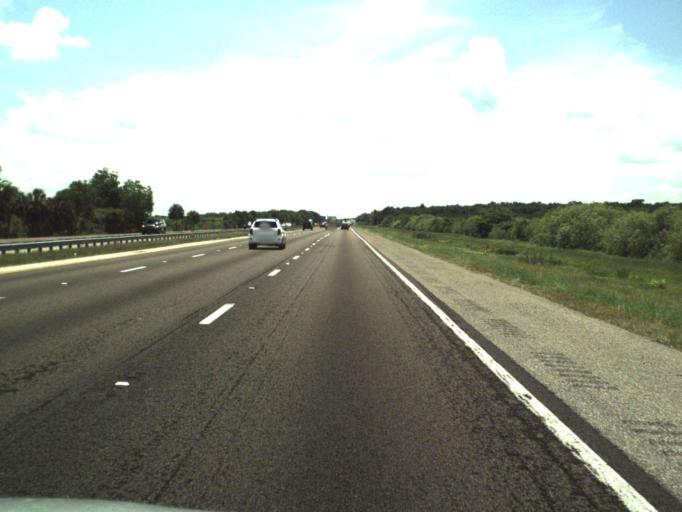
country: US
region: Florida
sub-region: Volusia County
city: DeBary
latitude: 28.8559
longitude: -81.2990
